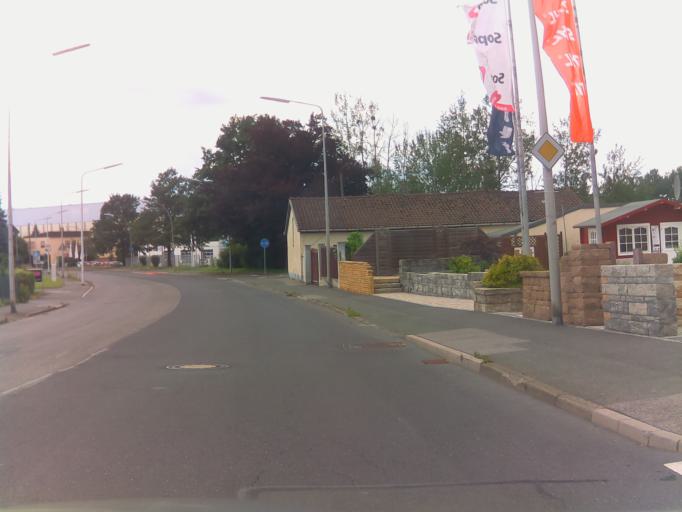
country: DE
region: Bavaria
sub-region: Upper Franconia
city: Neustadt bei Coburg
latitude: 50.3234
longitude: 11.1173
